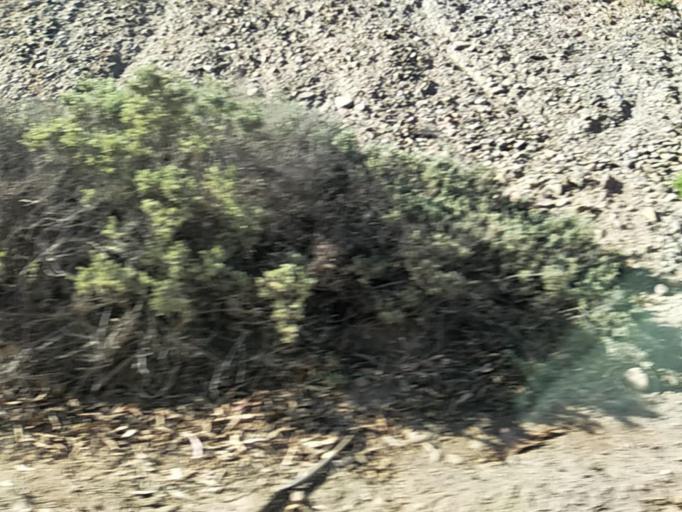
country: CL
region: Atacama
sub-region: Provincia de Copiapo
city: Copiapo
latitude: -27.3353
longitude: -70.7758
